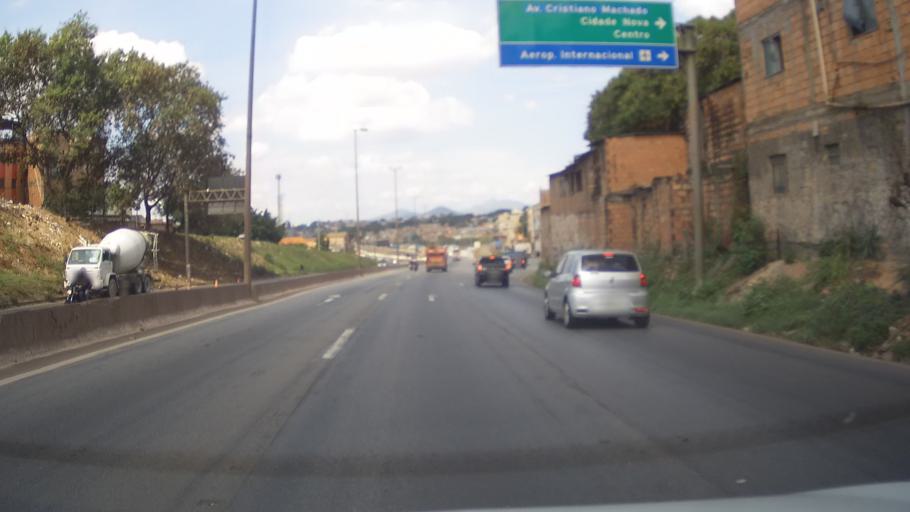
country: BR
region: Minas Gerais
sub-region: Belo Horizonte
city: Belo Horizonte
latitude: -19.8675
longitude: -43.9346
